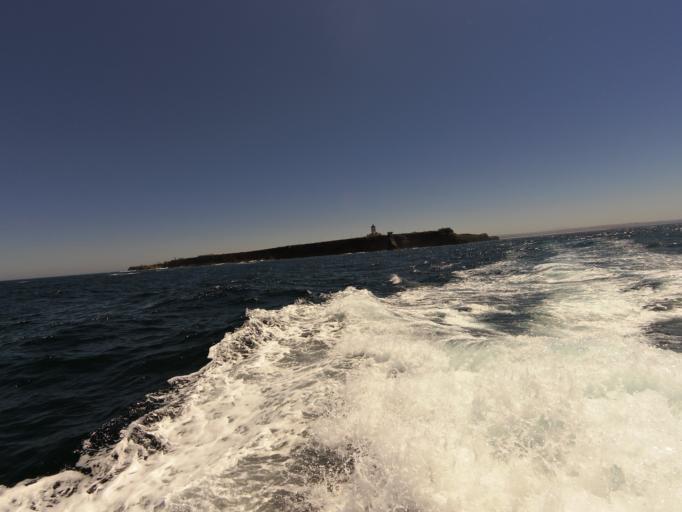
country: PT
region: Leiria
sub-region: Peniche
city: Peniche
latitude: 39.3612
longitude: -9.4162
